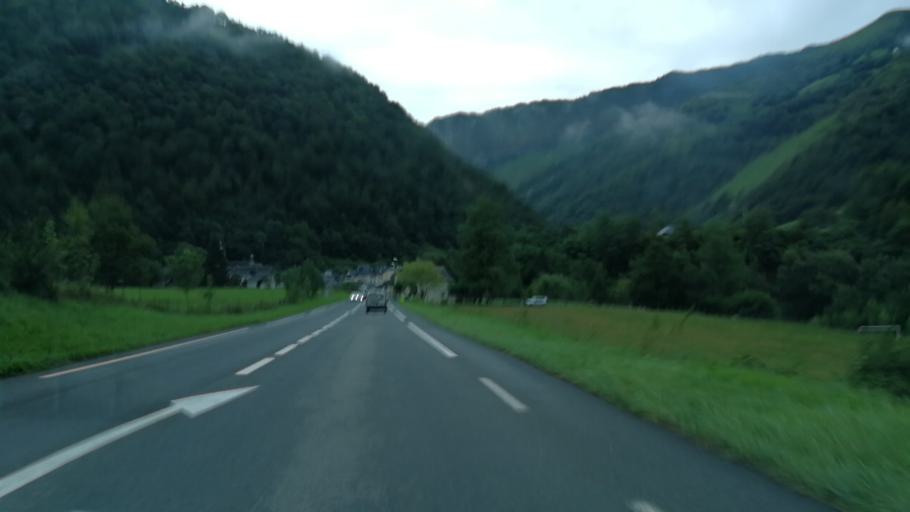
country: FR
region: Aquitaine
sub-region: Departement des Pyrenees-Atlantiques
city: Arette
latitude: 43.0477
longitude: -0.6010
